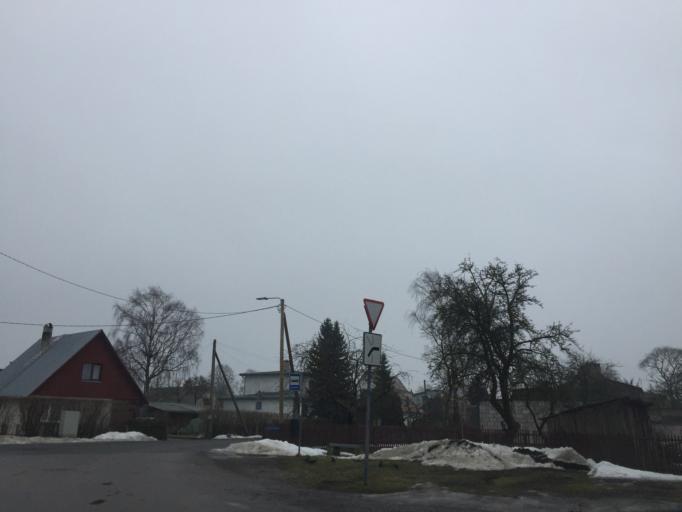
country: EE
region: Saare
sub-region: Kuressaare linn
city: Kuressaare
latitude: 58.2473
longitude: 22.4895
